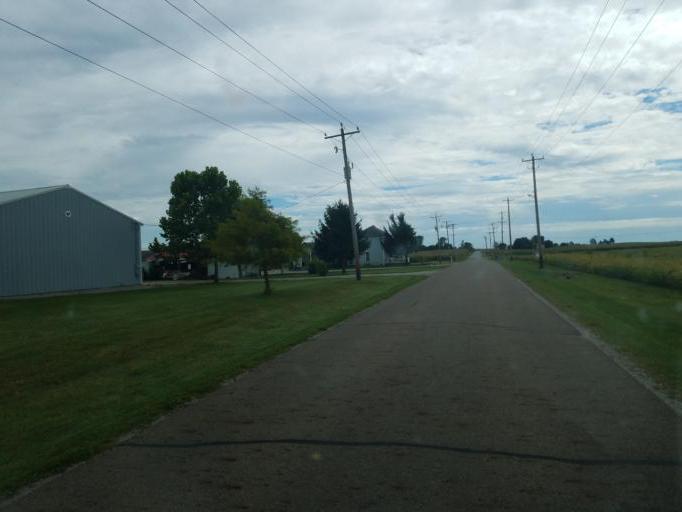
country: US
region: Ohio
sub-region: Knox County
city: Centerburg
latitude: 40.2464
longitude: -82.7148
